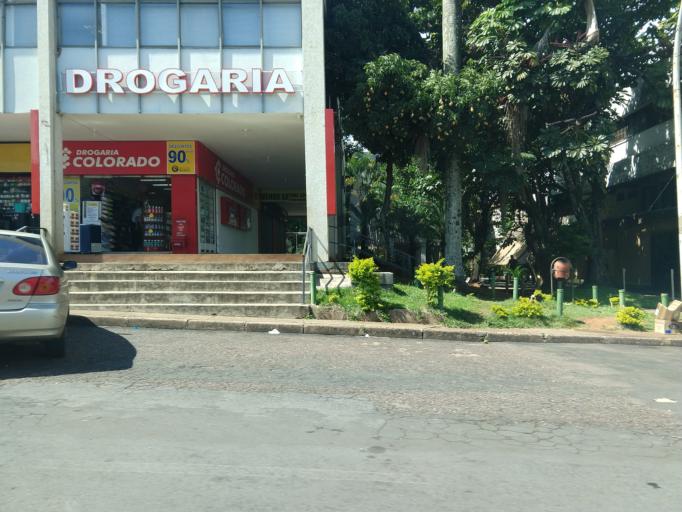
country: BR
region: Federal District
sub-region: Brasilia
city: Brasilia
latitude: -15.7800
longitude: -47.8761
